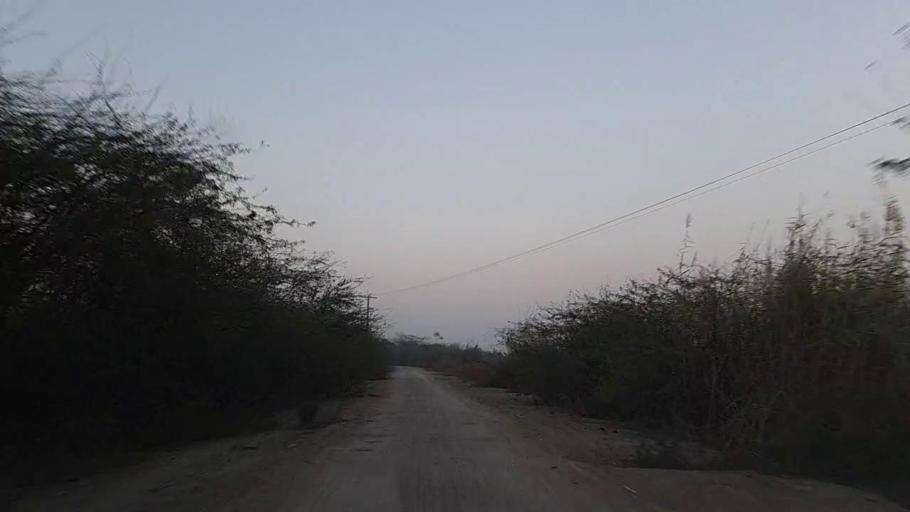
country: PK
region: Sindh
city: Bandhi
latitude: 26.6172
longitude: 68.3752
